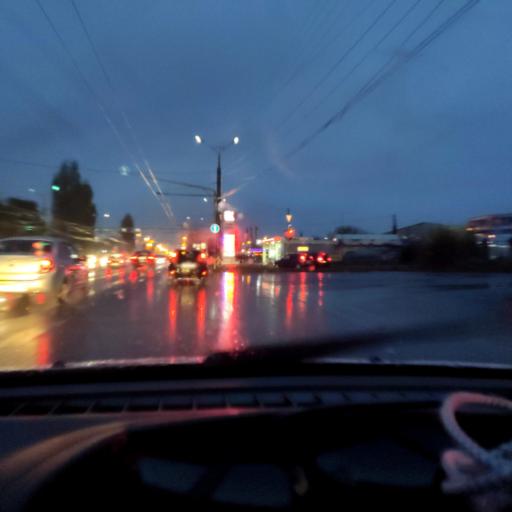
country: RU
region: Samara
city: Tol'yatti
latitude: 53.5356
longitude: 49.3947
